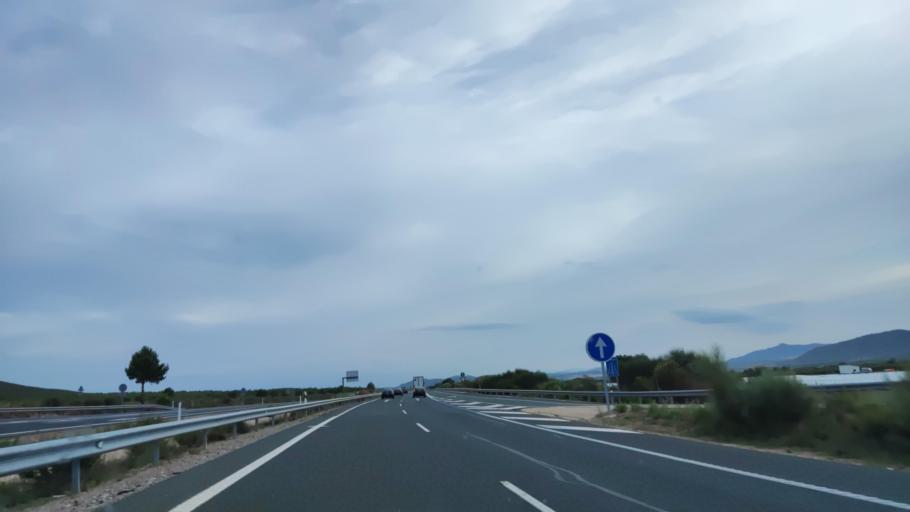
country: ES
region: Castille-La Mancha
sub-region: Provincia de Albacete
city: Tobarra
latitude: 38.6326
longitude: -1.6694
